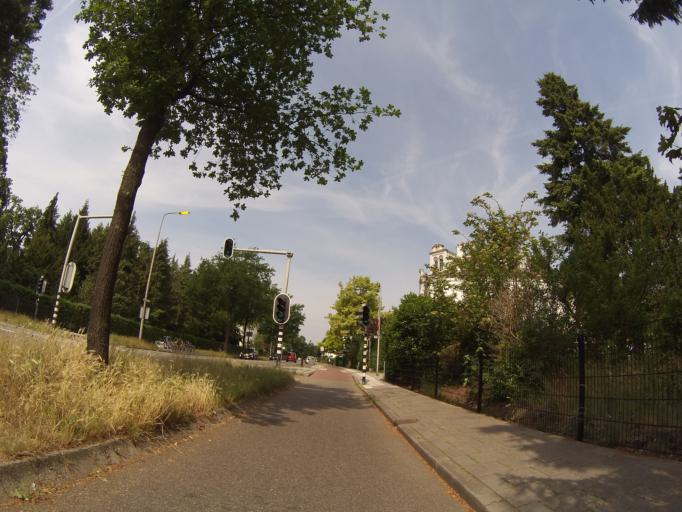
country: NL
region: Utrecht
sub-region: Gemeente Zeist
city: Zeist
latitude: 52.0856
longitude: 5.2346
